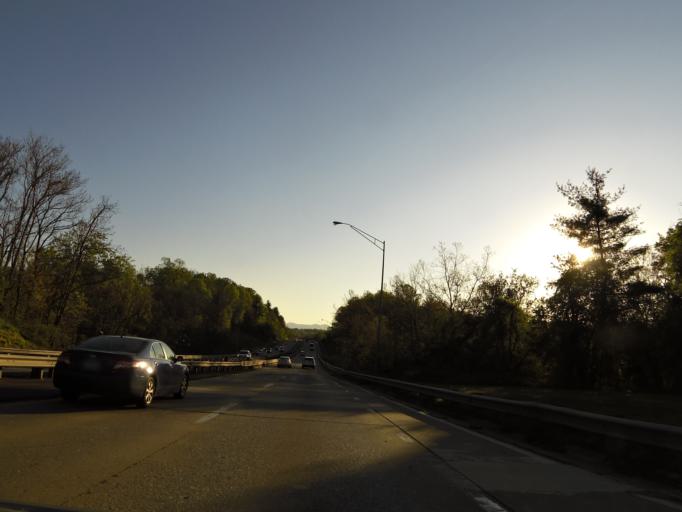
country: US
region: North Carolina
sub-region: Buncombe County
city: Bent Creek
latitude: 35.5633
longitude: -82.5962
